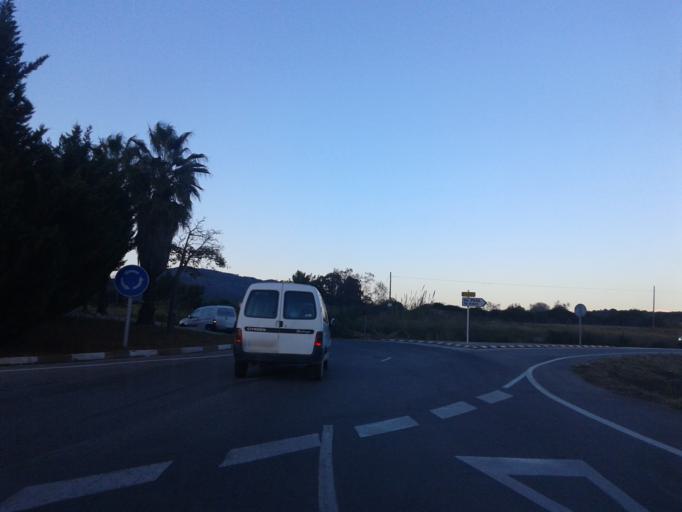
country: ES
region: Catalonia
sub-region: Provincia de Barcelona
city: Vilanova i la Geltru
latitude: 41.2373
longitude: 1.7339
